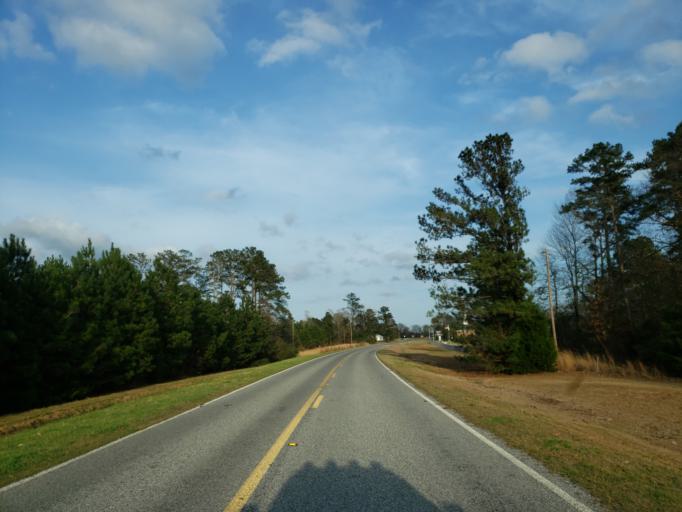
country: US
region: Mississippi
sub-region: Clarke County
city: Stonewall
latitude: 32.1732
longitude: -88.6844
